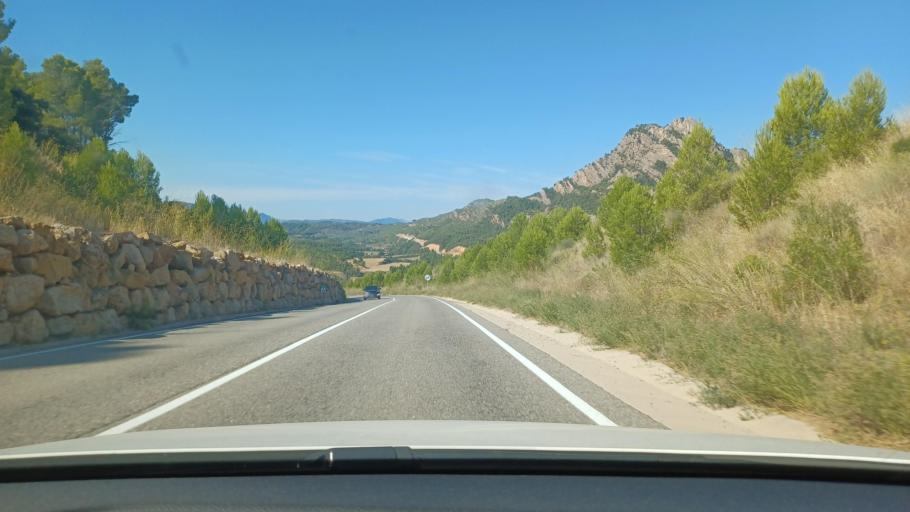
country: ES
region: Catalonia
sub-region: Provincia de Tarragona
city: Horta de Sant Joan
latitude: 40.9630
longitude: 0.3641
